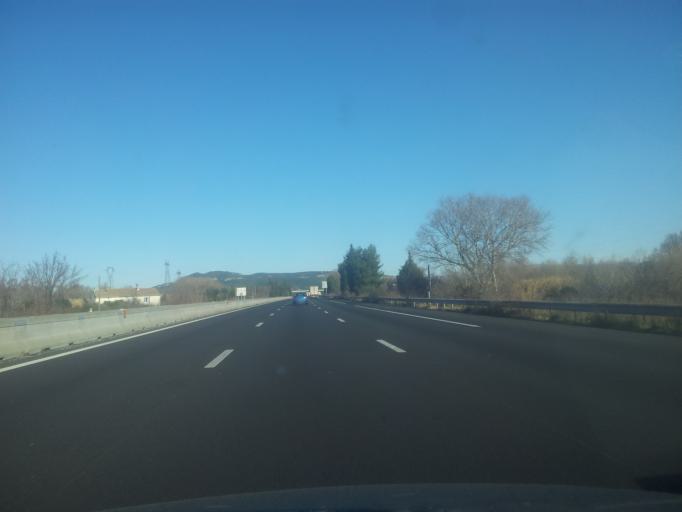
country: FR
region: Provence-Alpes-Cote d'Azur
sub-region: Departement du Vaucluse
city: Bollene
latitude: 44.2790
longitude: 4.7323
